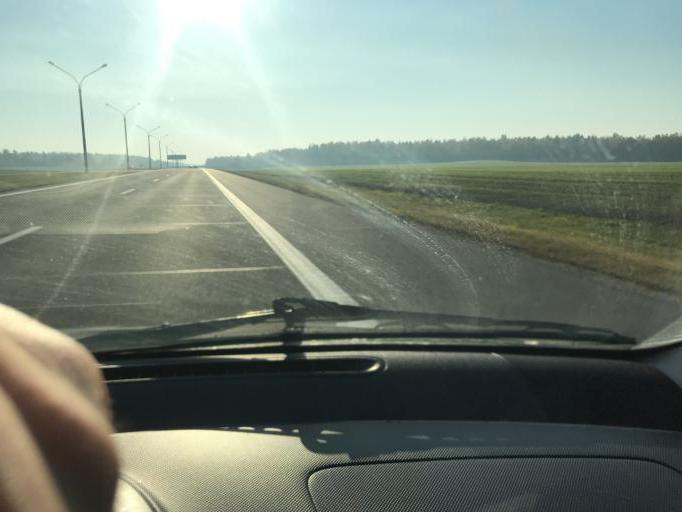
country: BY
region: Minsk
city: Slabada
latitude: 53.9750
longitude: 27.9421
